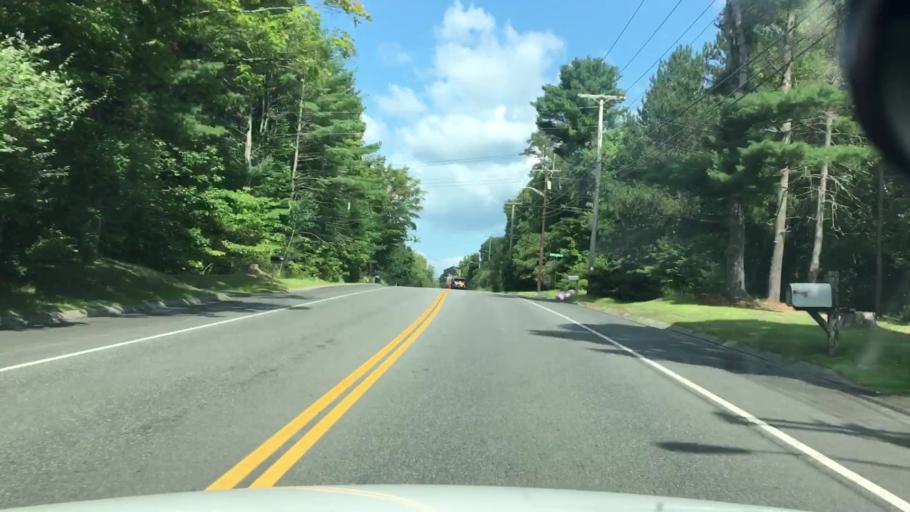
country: US
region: Maine
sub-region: Kennebec County
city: Waterville
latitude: 44.5793
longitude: -69.6461
